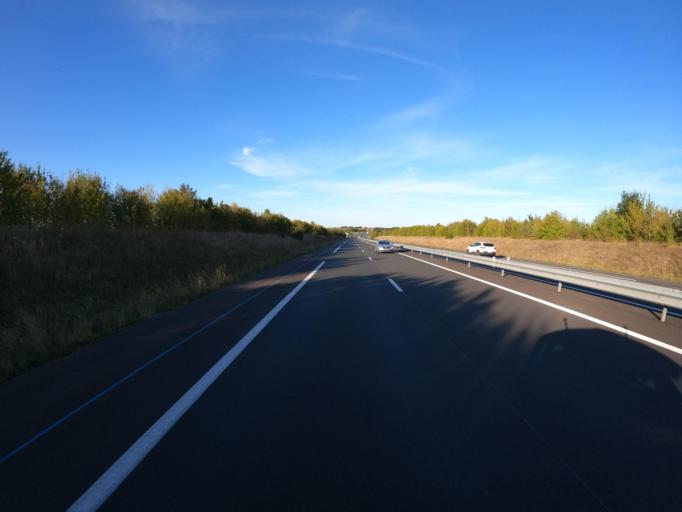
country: FR
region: Pays de la Loire
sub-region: Departement de la Vendee
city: Mortagne-sur-Sevre
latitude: 46.9943
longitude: -0.9126
